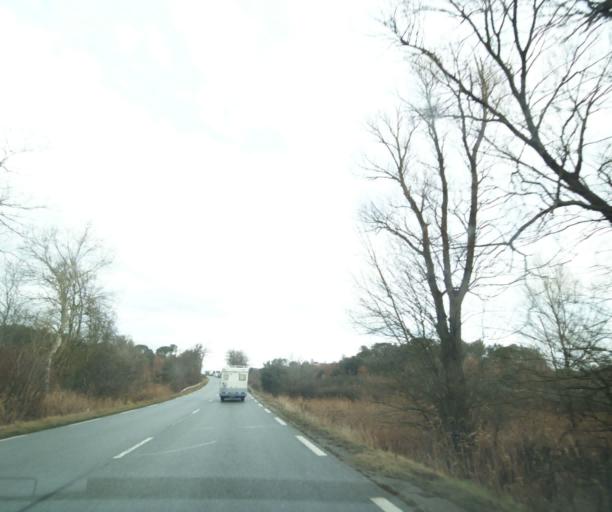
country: FR
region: Provence-Alpes-Cote d'Azur
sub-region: Departement du Var
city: Tourves
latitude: 43.4159
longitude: 5.9089
